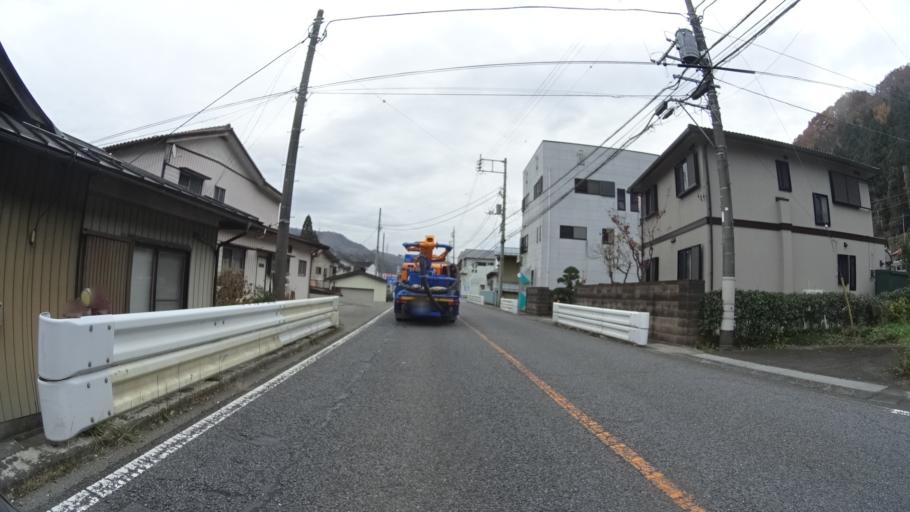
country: JP
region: Gunma
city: Numata
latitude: 36.6054
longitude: 139.0456
